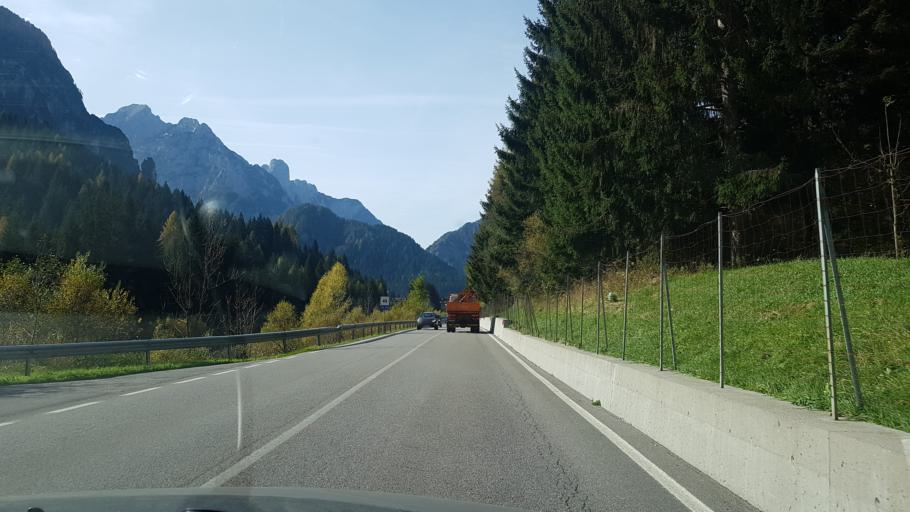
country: IT
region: Veneto
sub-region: Provincia di Belluno
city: Santo Stefano di Cadore
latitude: 46.5618
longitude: 12.5669
